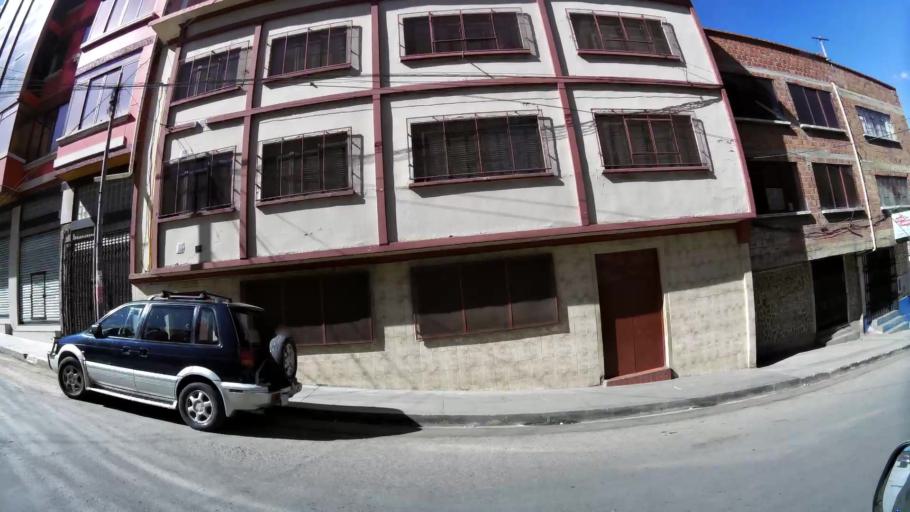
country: BO
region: La Paz
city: La Paz
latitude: -16.5113
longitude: -68.1426
